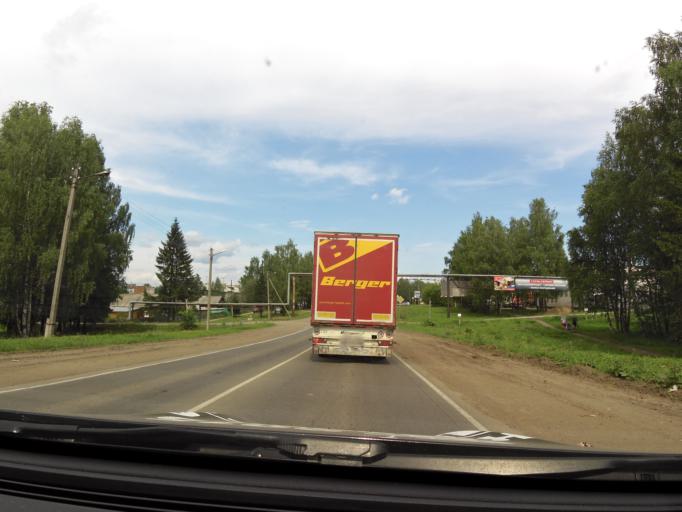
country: RU
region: Kirov
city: Stulovo
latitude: 58.7180
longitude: 50.1320
